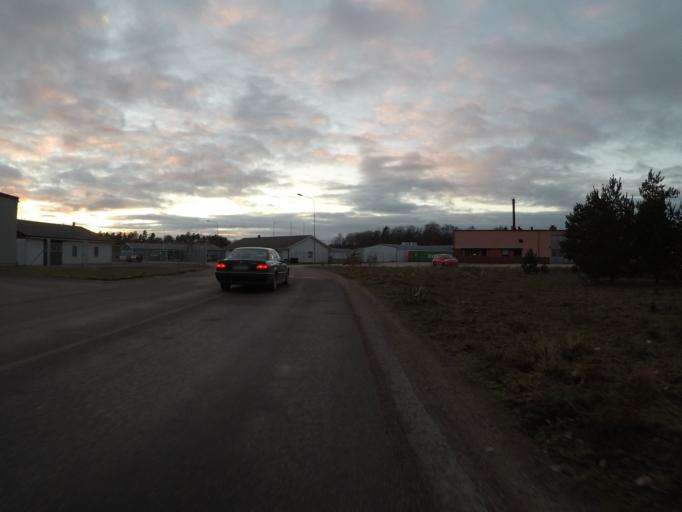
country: SE
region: Skane
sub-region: Sjobo Kommun
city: Sjoebo
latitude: 55.6413
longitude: 13.6886
